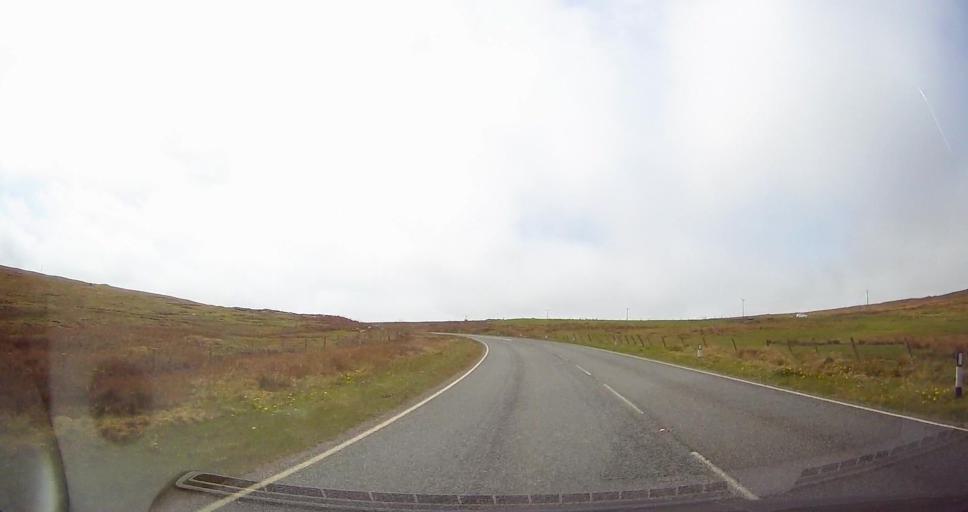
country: GB
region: Scotland
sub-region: Shetland Islands
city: Sandwick
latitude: 60.0106
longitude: -1.2591
